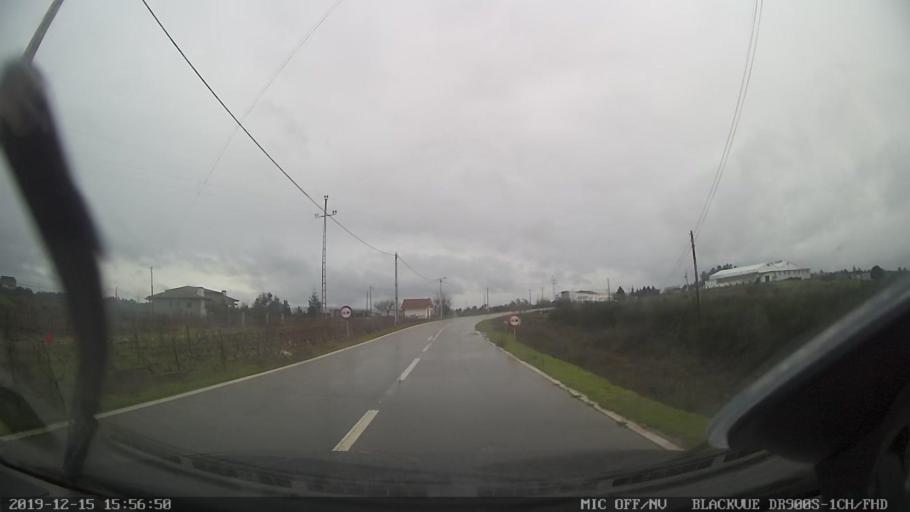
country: PT
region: Vila Real
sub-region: Sabrosa
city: Vilela
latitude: 41.2020
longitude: -7.6824
